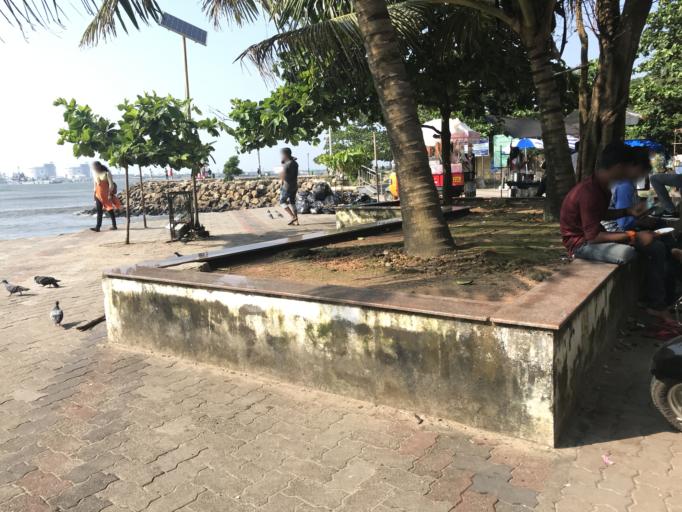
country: IN
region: Kerala
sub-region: Ernakulam
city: Cochin
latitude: 9.9637
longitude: 76.2379
